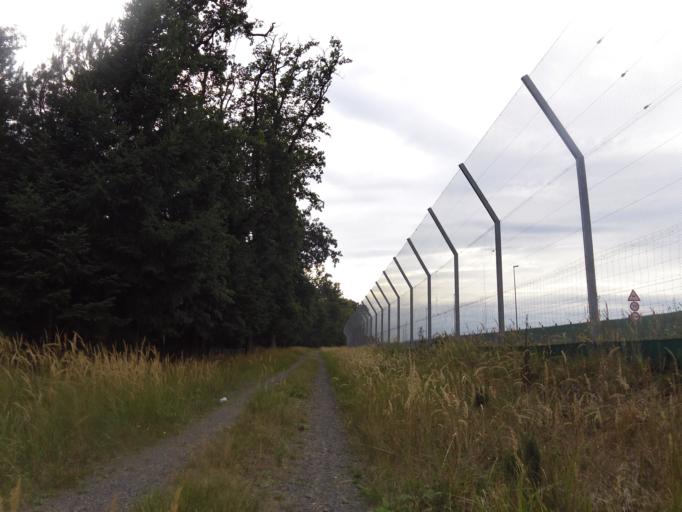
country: DE
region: Hesse
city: Kelsterbach
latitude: 50.0229
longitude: 8.5421
